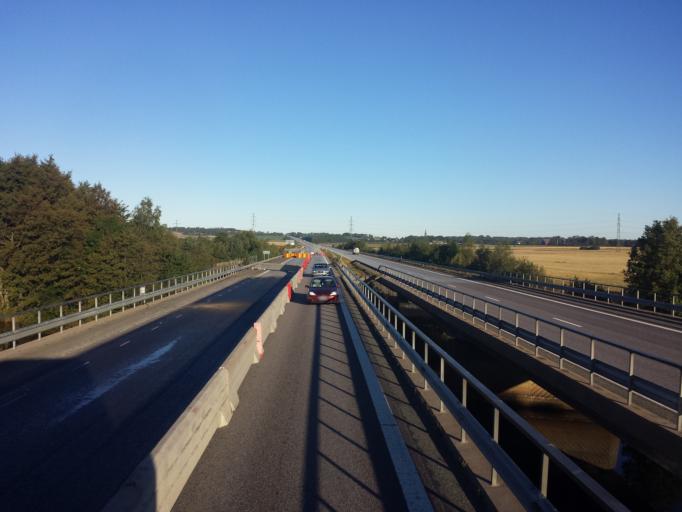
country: SE
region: Halland
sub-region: Falkenbergs Kommun
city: Falkenberg
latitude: 56.9075
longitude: 12.5714
